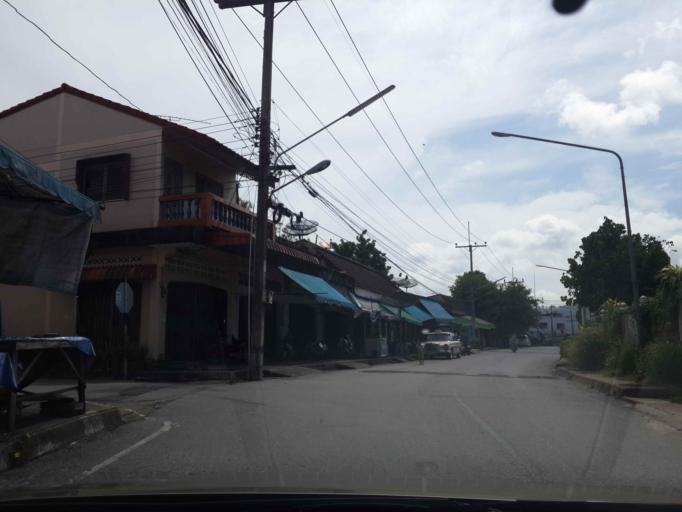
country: TH
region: Narathiwat
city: Rueso
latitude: 6.3959
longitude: 101.5170
